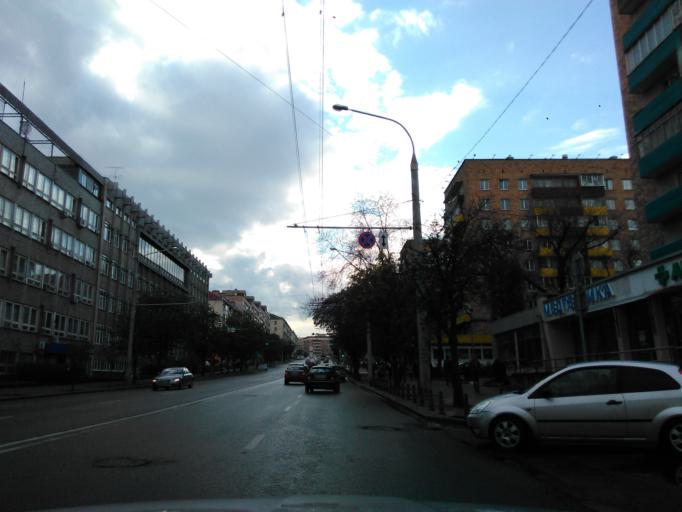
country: BY
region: Minsk
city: Minsk
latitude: 53.9026
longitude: 27.5470
